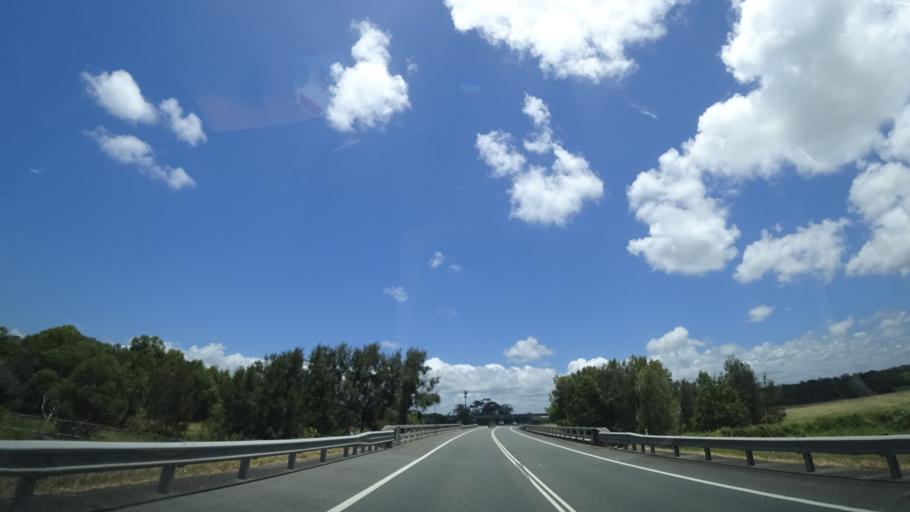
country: AU
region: Queensland
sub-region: Sunshine Coast
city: Little Mountain
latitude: -26.7645
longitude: 153.1039
